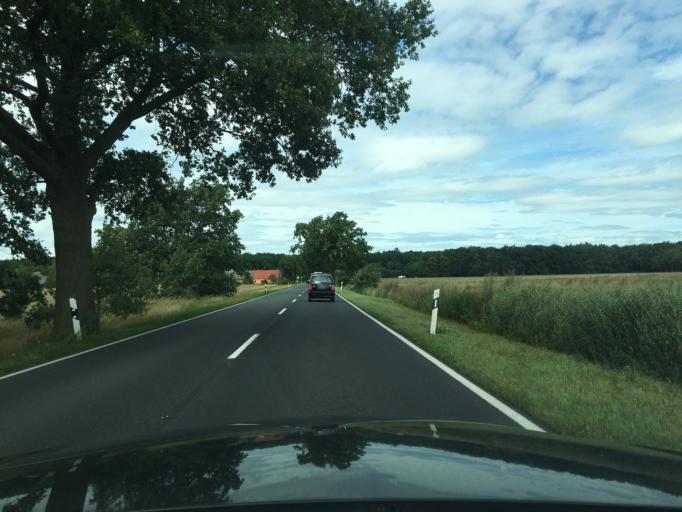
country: DE
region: Brandenburg
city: Gransee
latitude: 53.0535
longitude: 13.1923
